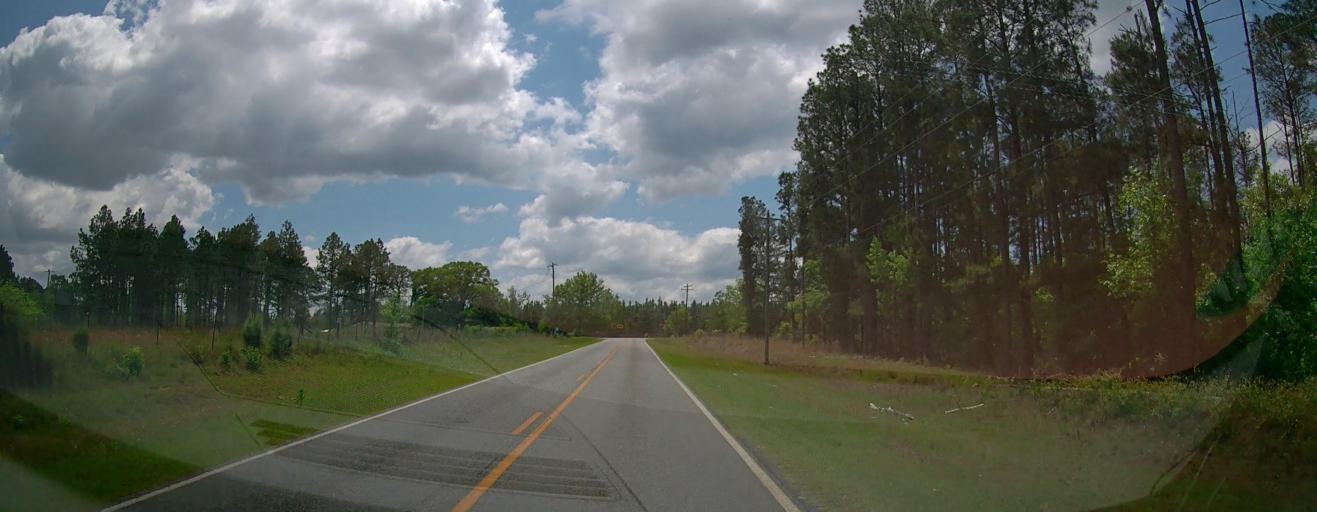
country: US
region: Georgia
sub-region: Laurens County
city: East Dublin
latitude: 32.5695
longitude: -82.8005
